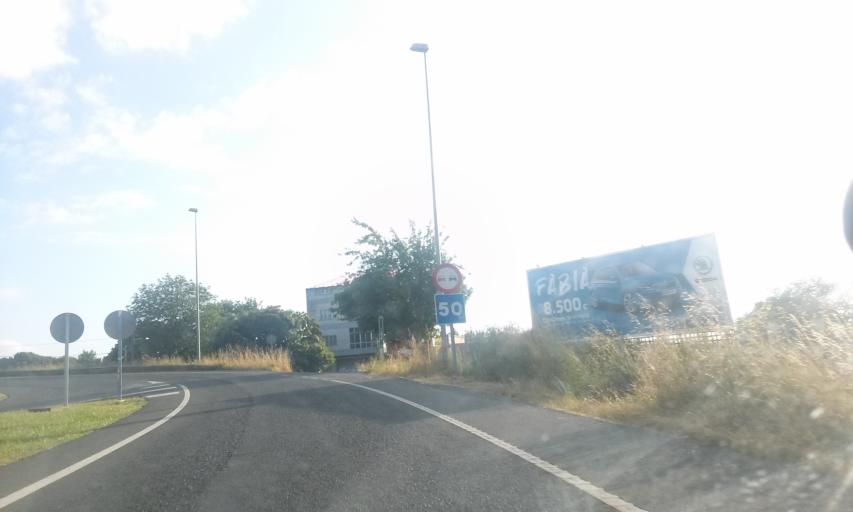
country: ES
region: Galicia
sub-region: Provincia de Lugo
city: Lugo
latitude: 43.0298
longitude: -7.5742
